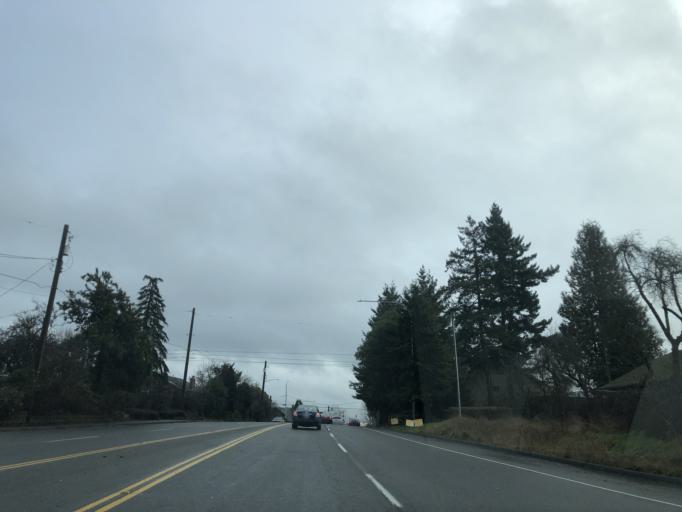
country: US
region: Washington
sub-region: Pierce County
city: Tacoma
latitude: 47.2230
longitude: -122.4602
